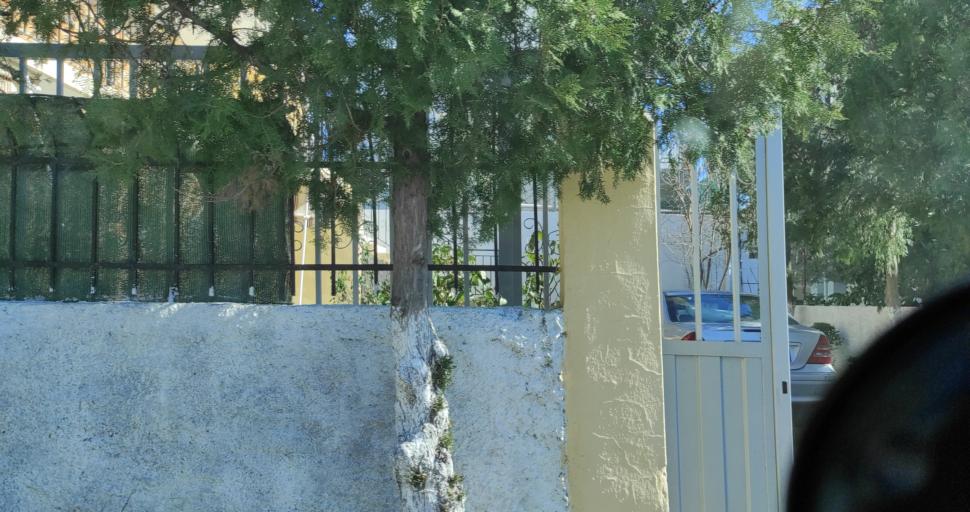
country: AL
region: Shkoder
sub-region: Rrethi i Shkodres
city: Velipoje
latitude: 41.8658
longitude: 19.4227
